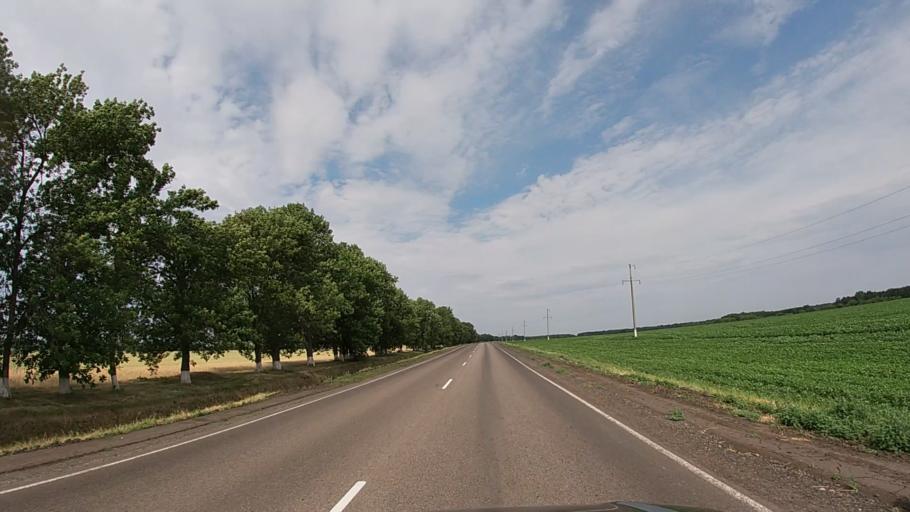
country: RU
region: Belgorod
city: Krasnaya Yaruga
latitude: 50.8082
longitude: 35.5347
